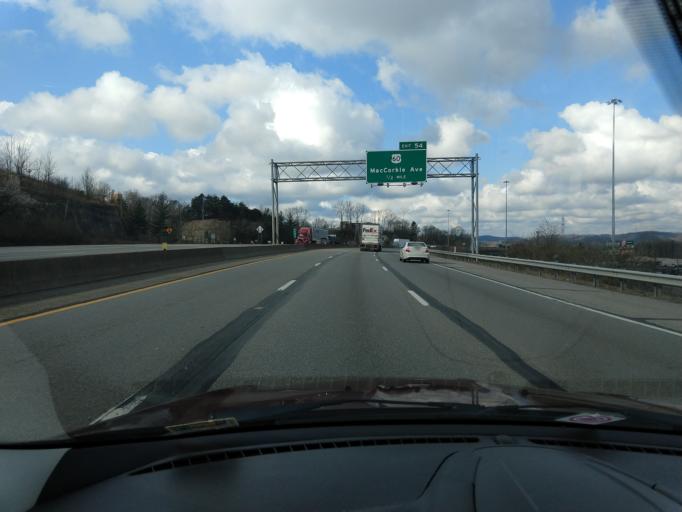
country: US
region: West Virginia
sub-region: Kanawha County
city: South Charleston
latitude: 38.3602
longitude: -81.7000
